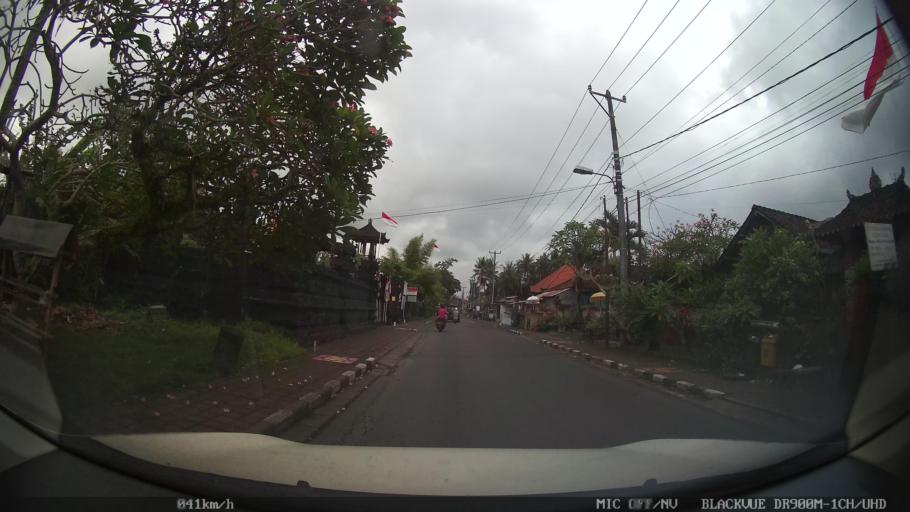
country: ID
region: Bali
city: Banjar Cemenggon
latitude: -8.5412
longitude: 115.2067
